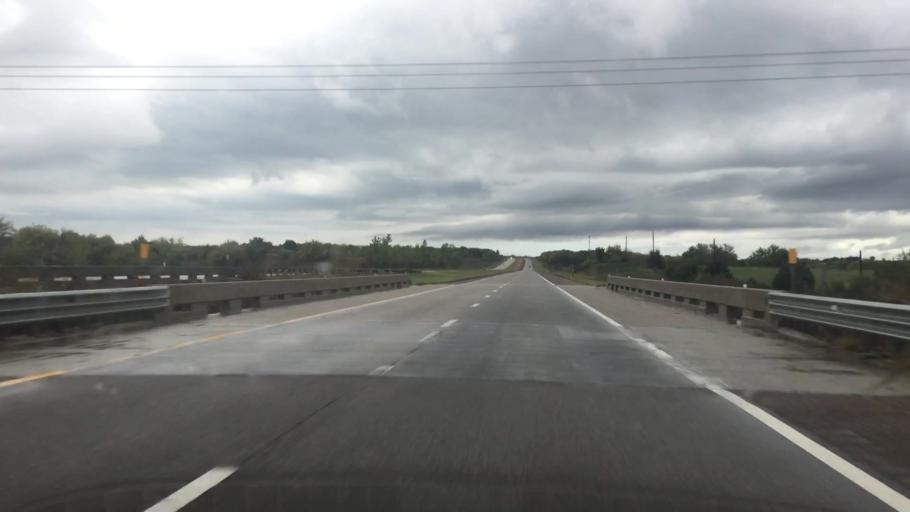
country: US
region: Kansas
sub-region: Miami County
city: Paola
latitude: 38.6070
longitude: -94.8356
